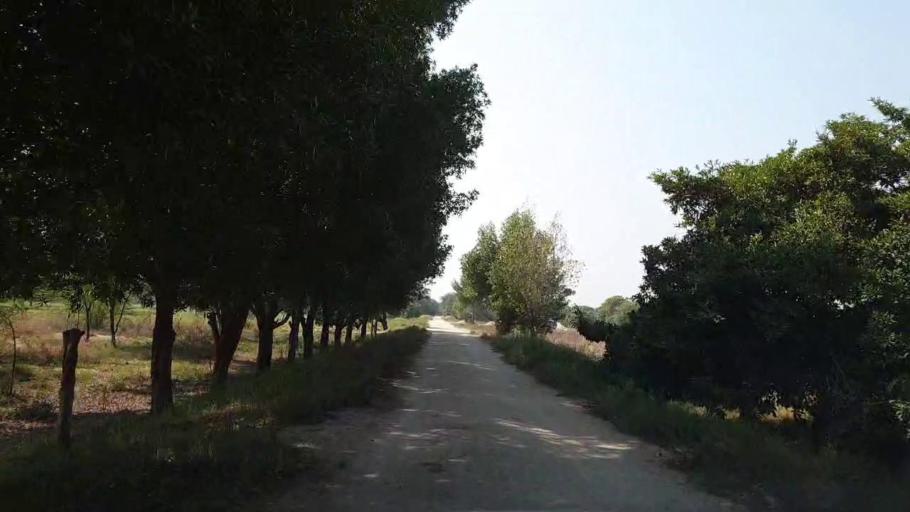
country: PK
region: Sindh
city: Mirpur Khas
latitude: 25.6271
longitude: 69.1069
